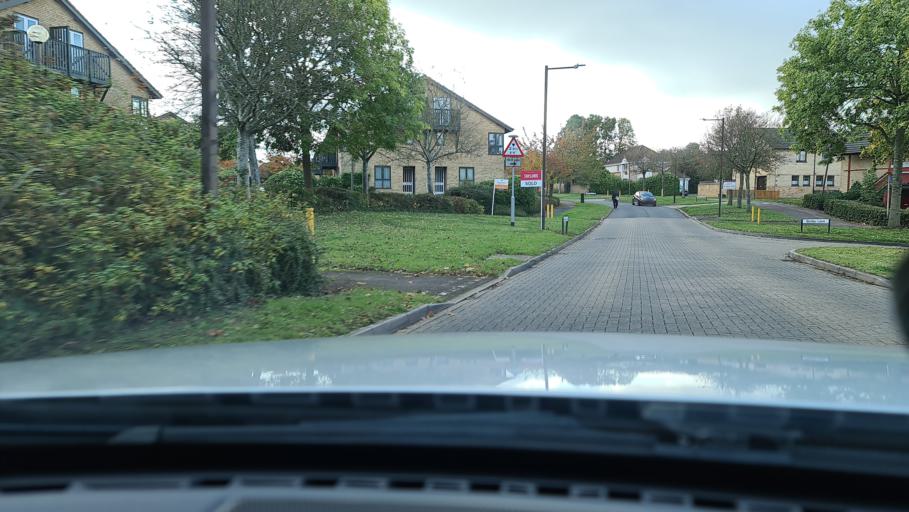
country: GB
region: England
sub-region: Milton Keynes
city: Simpson
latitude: 52.0242
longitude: -0.6946
